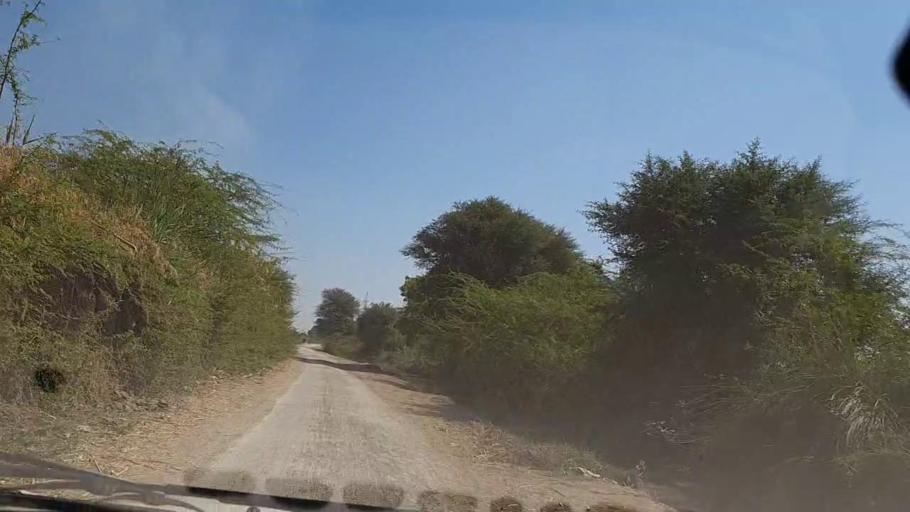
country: PK
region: Sindh
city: Mirpur Khas
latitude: 25.4296
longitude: 69.0237
